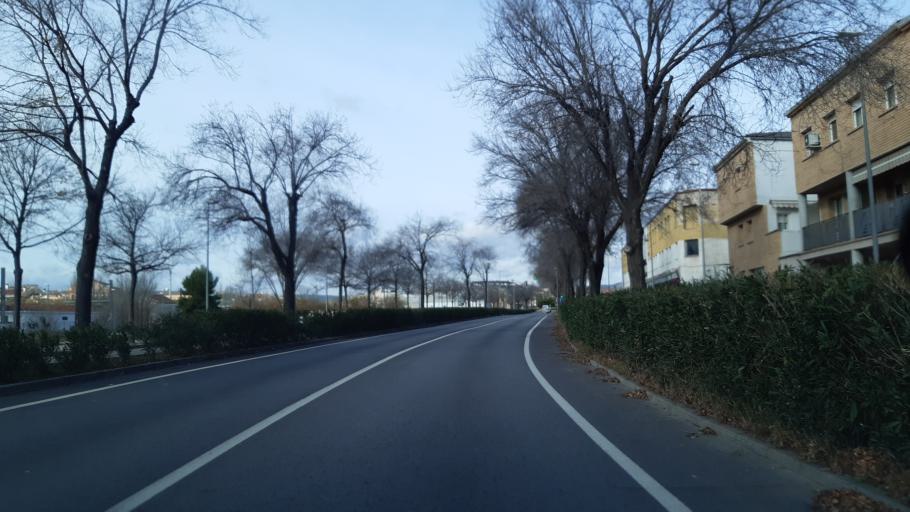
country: ES
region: Catalonia
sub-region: Provincia de Barcelona
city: Vilanova del Cami
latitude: 41.5727
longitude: 1.6443
